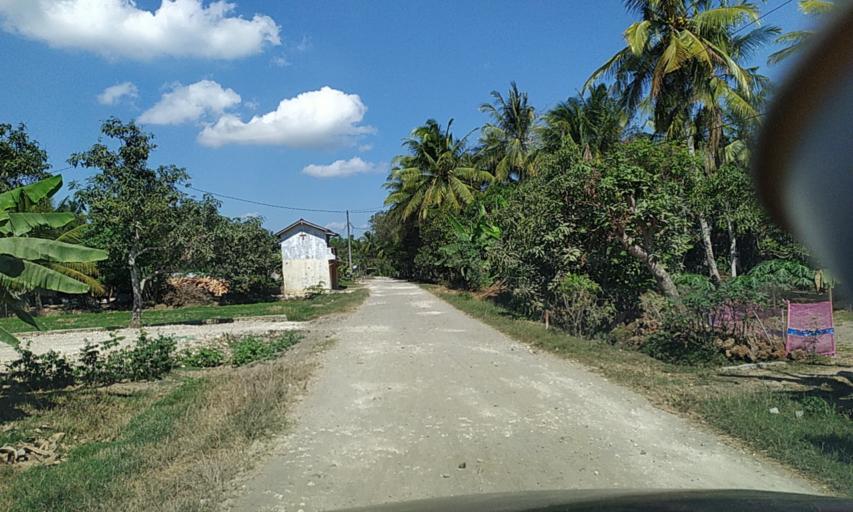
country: ID
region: Central Java
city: Kalenaren
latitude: -7.5822
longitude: 108.8033
